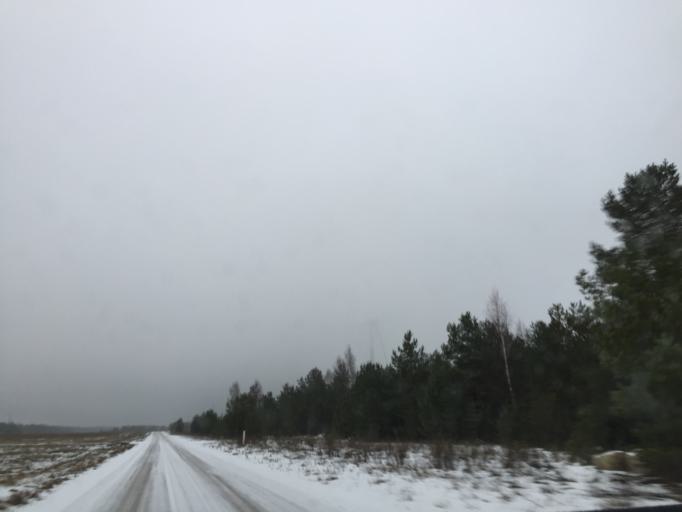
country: EE
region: Laeaene
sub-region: Lihula vald
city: Lihula
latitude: 58.6261
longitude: 23.5372
